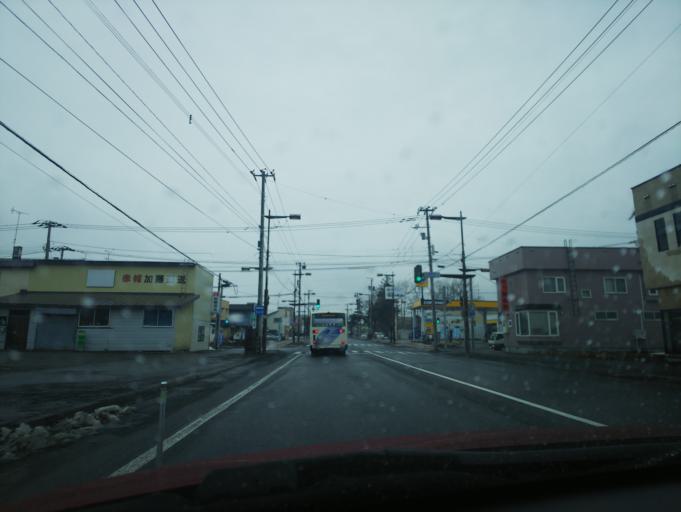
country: JP
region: Hokkaido
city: Nayoro
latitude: 44.1697
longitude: 142.3942
